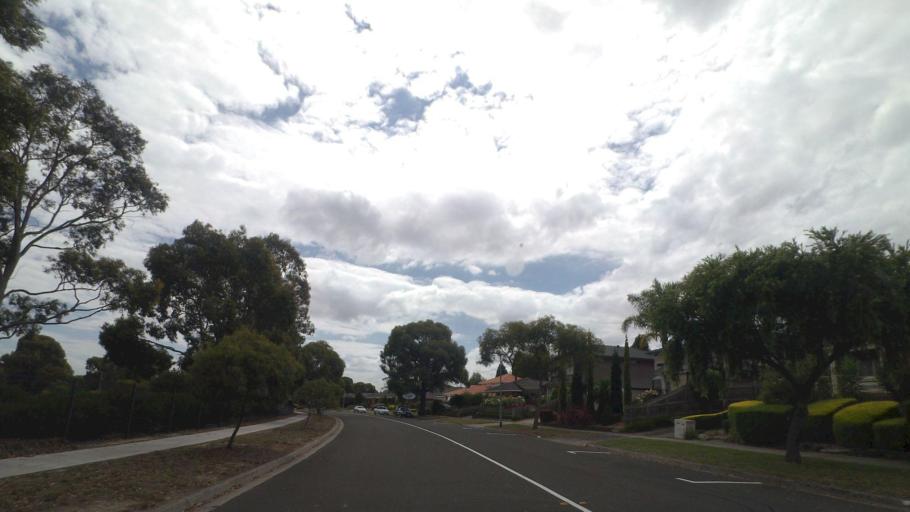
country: AU
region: Victoria
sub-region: Knox
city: Wantirna South
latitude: -37.8806
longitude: 145.2293
